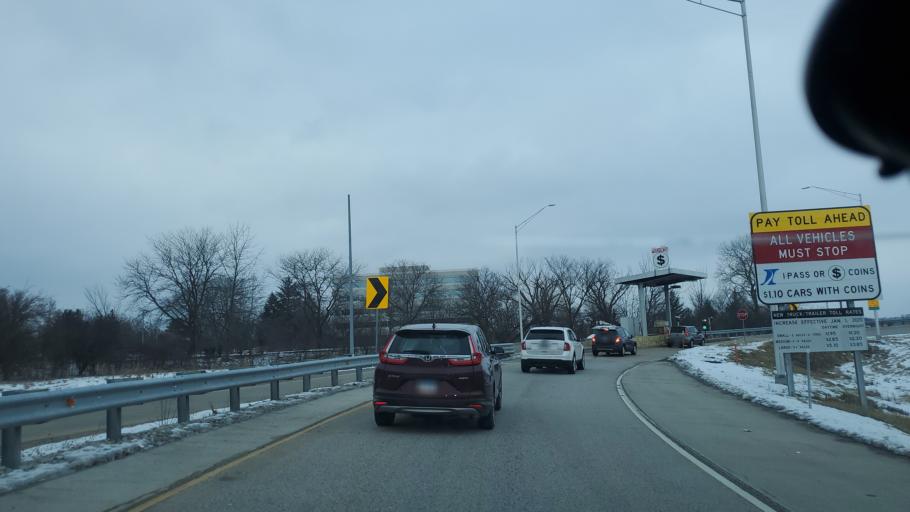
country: US
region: Illinois
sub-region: Kane County
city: North Aurora
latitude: 41.7993
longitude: -88.2839
